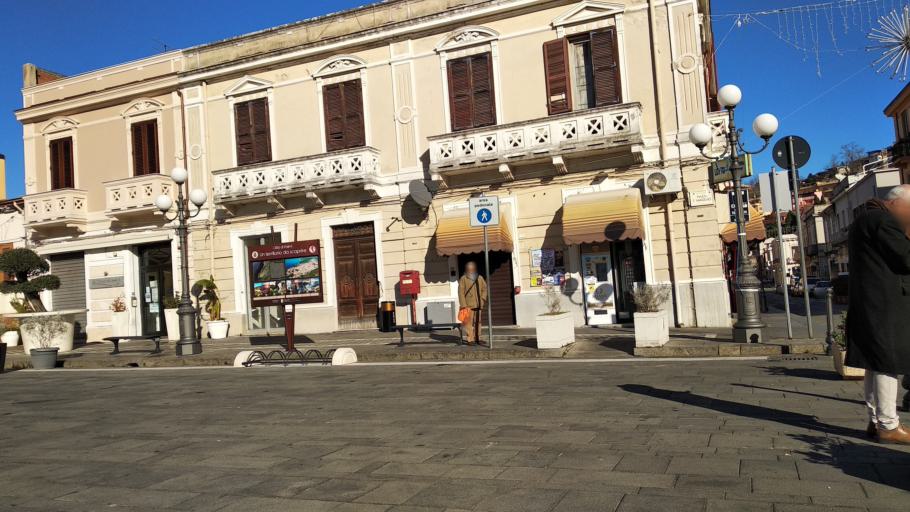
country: IT
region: Calabria
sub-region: Provincia di Reggio Calabria
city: Seminara
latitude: 38.3566
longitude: 15.8473
